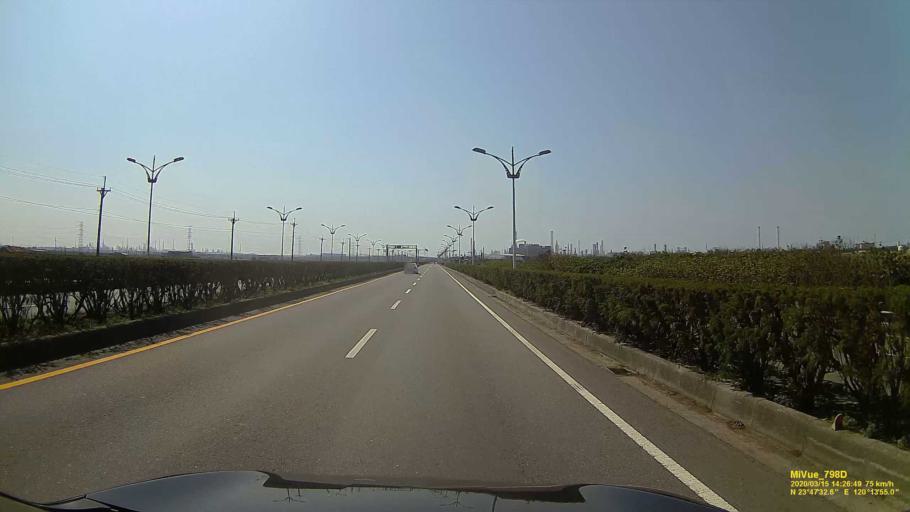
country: TW
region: Taiwan
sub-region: Yunlin
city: Douliu
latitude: 23.7924
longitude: 120.2316
